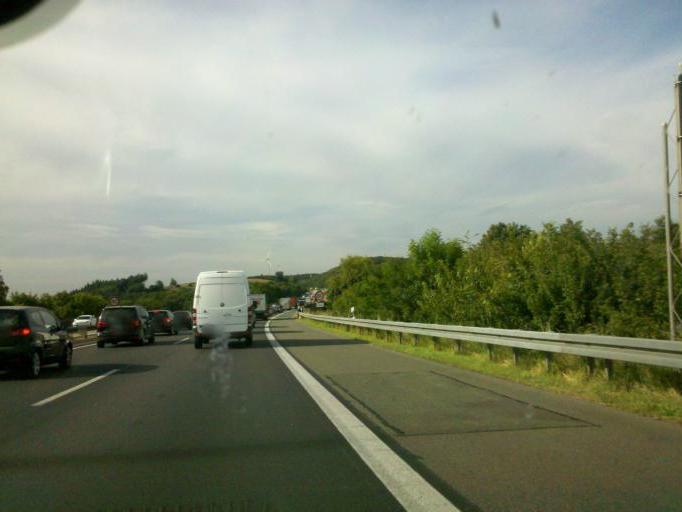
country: DE
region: North Rhine-Westphalia
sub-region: Regierungsbezirk Arnsberg
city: Nachrodt-Wiblingwerde
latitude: 51.2979
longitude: 7.5534
